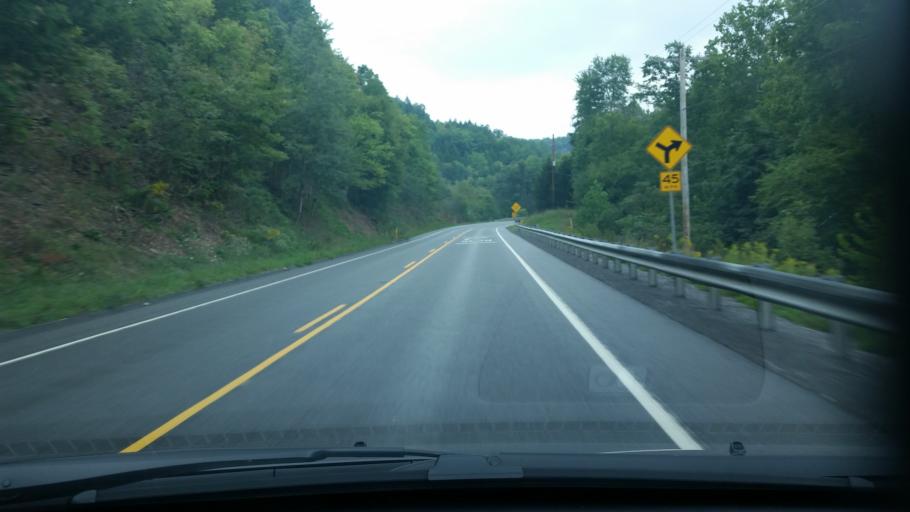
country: US
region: Pennsylvania
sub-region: Clearfield County
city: Shiloh
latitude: 41.0902
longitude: -78.2453
